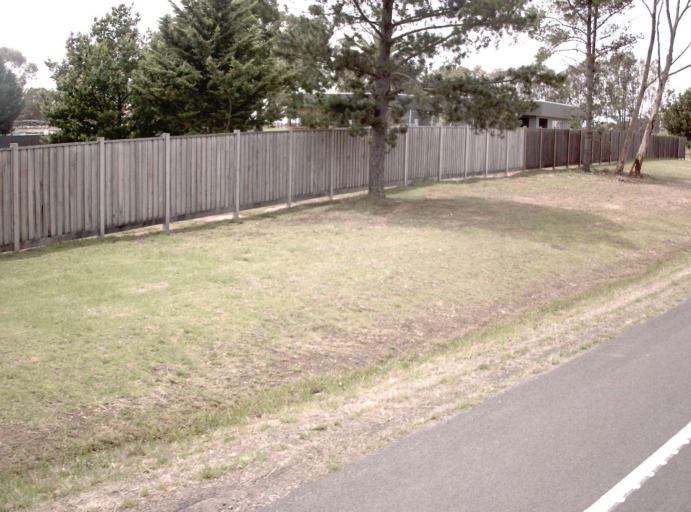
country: AU
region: Victoria
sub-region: Wellington
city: Sale
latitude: -38.0654
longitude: 147.0302
